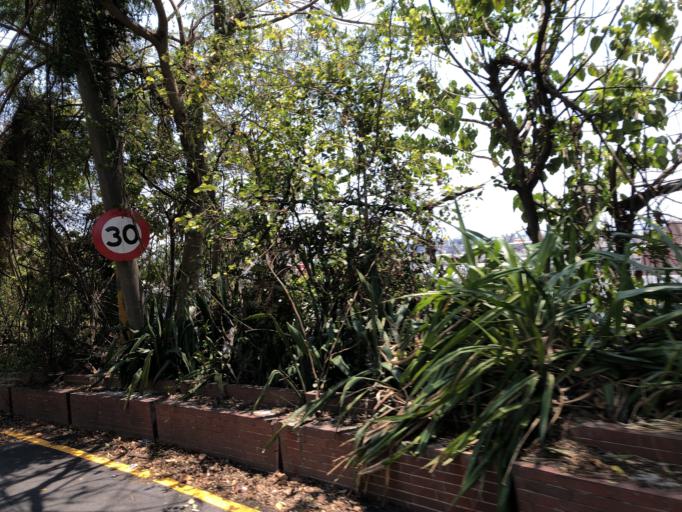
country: TW
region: Kaohsiung
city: Kaohsiung
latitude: 22.6262
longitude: 120.2713
